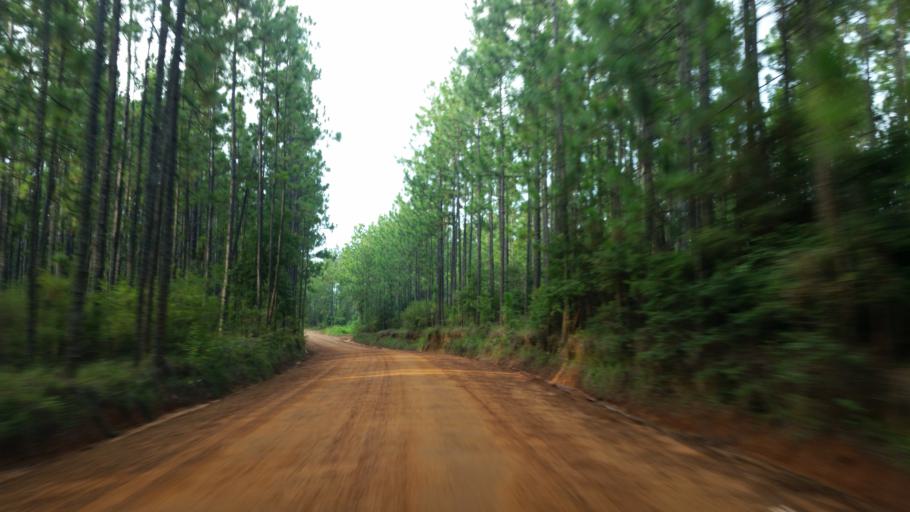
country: US
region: Alabama
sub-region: Escambia County
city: Atmore
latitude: 30.9391
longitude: -87.5720
